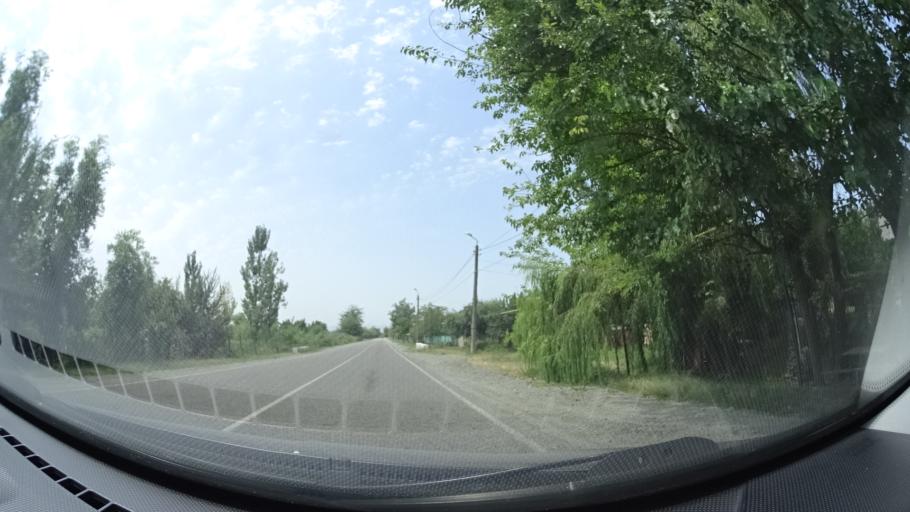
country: GE
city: Bagdadi
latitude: 41.7719
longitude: 46.1386
